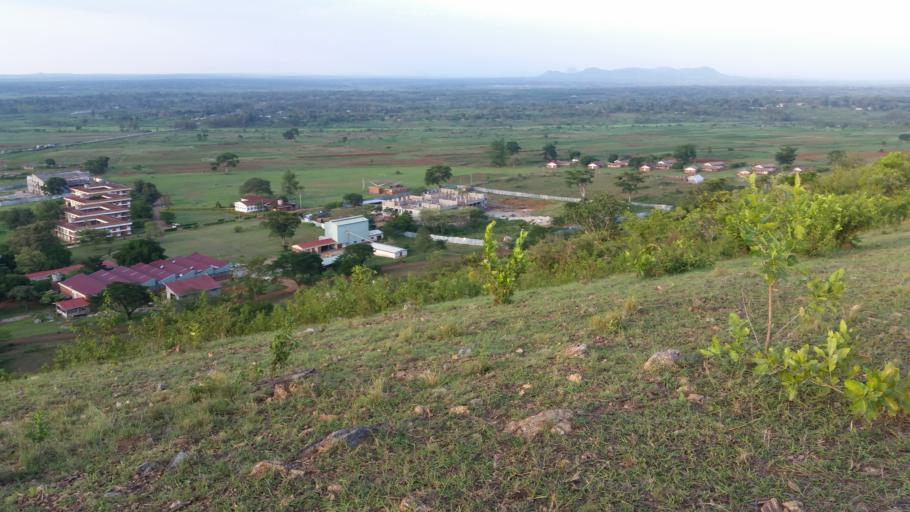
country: UG
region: Eastern Region
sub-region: Busia District
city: Busia
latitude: 0.5420
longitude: 34.0198
